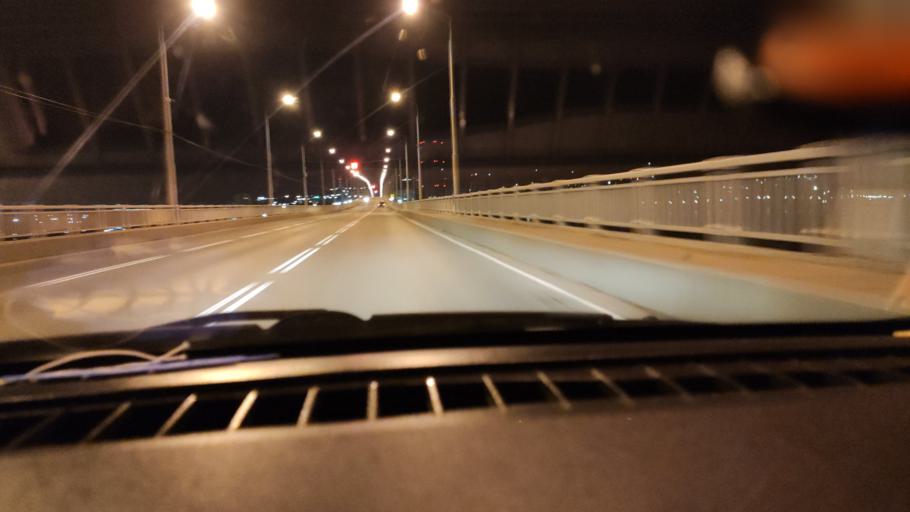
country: RU
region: Saratov
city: Engel's
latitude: 51.5187
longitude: 46.0708
